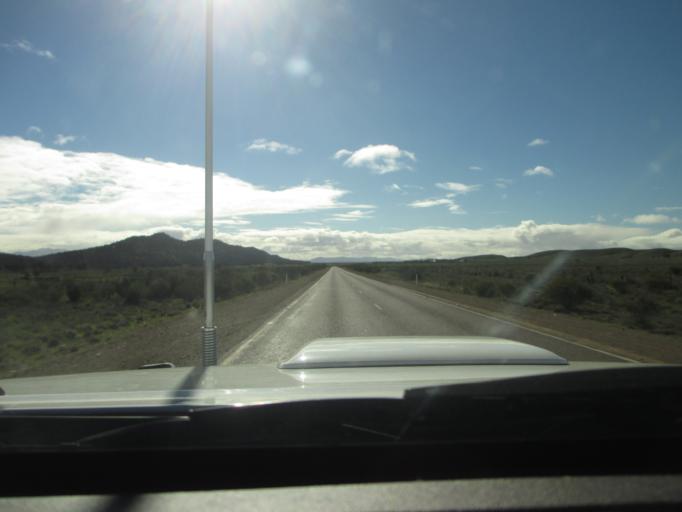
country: AU
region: South Australia
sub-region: Flinders Ranges
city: Quorn
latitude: -31.9466
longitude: 138.3991
